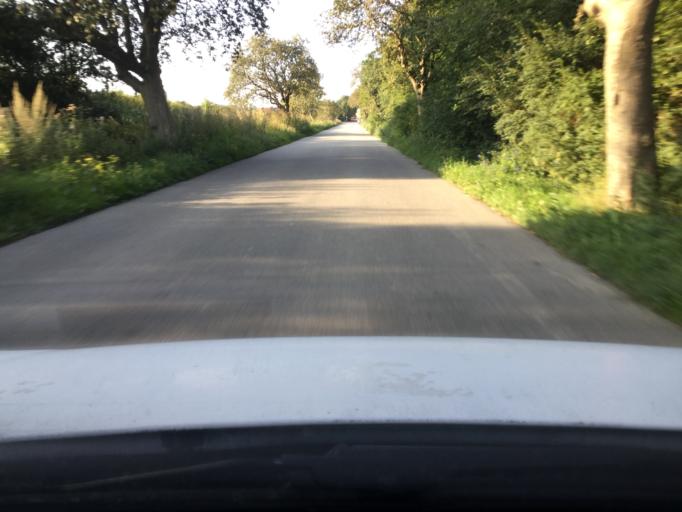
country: DK
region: Zealand
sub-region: Lolland Kommune
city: Rodby
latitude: 54.7003
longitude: 11.3882
